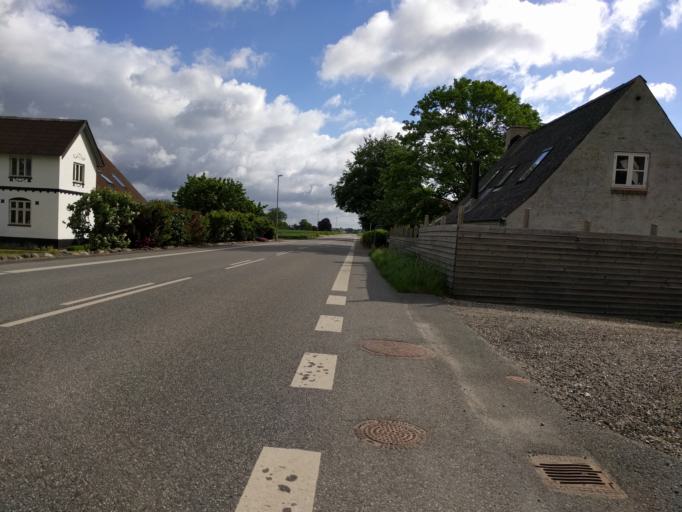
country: DK
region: South Denmark
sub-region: Kerteminde Kommune
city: Kerteminde
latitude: 55.4123
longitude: 10.6305
